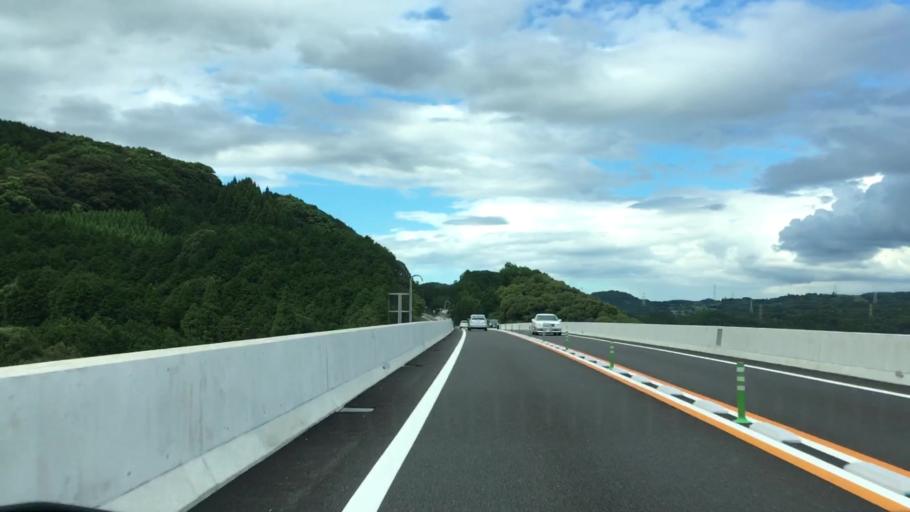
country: JP
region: Saga Prefecture
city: Imaricho-ko
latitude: 33.3242
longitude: 129.9269
